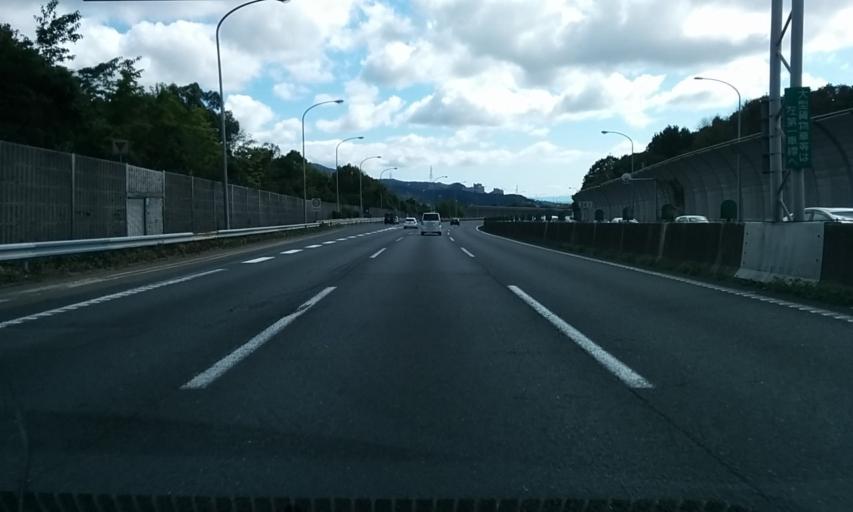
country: JP
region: Hyogo
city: Takarazuka
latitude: 34.8300
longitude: 135.2896
